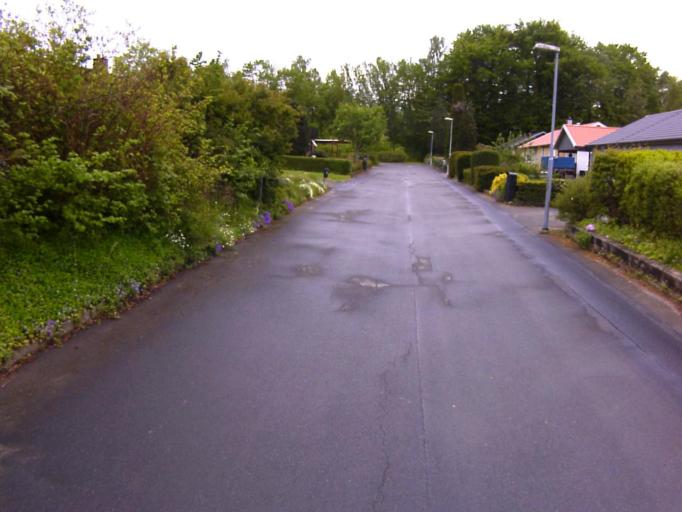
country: SE
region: Skane
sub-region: Kristianstads Kommun
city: Degeberga
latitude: 55.8280
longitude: 14.0795
